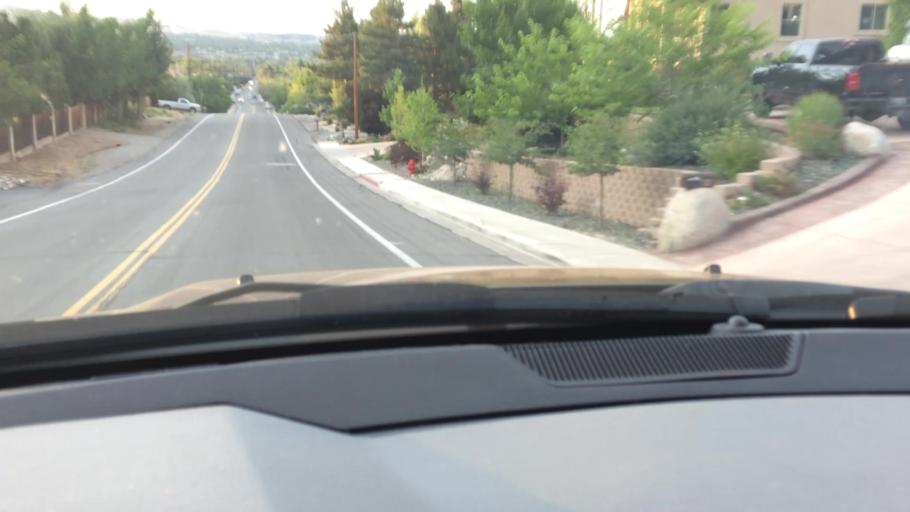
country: US
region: Nevada
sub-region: Washoe County
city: Reno
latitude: 39.5012
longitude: -119.8357
